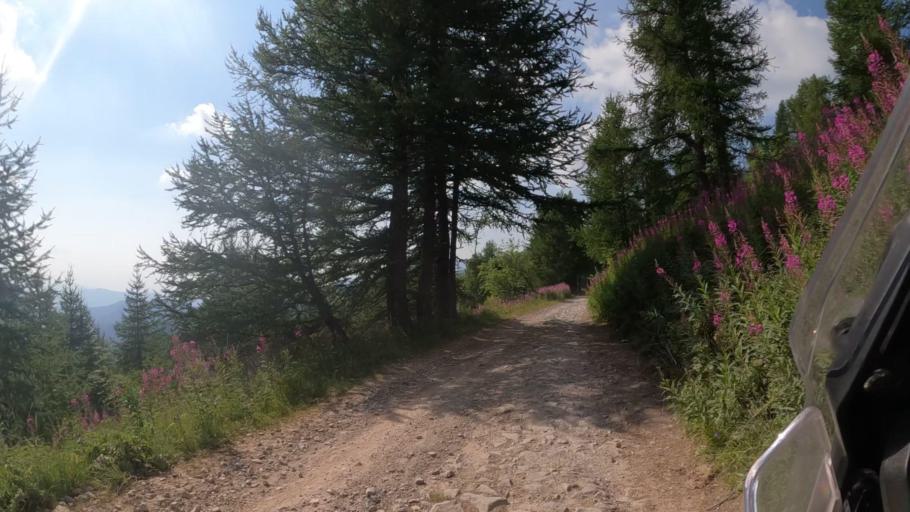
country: IT
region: Piedmont
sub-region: Provincia di Cuneo
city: Briga Alta
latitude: 44.1264
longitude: 7.6917
